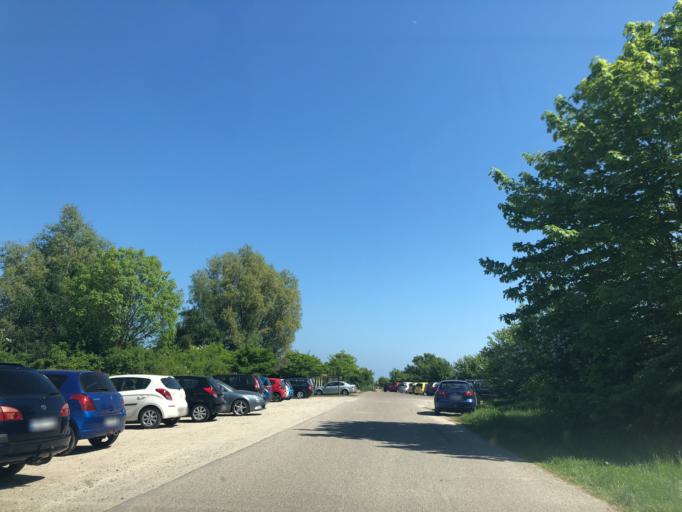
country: DK
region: Zealand
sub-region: Koge Kommune
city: Koge
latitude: 55.4909
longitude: 12.1984
